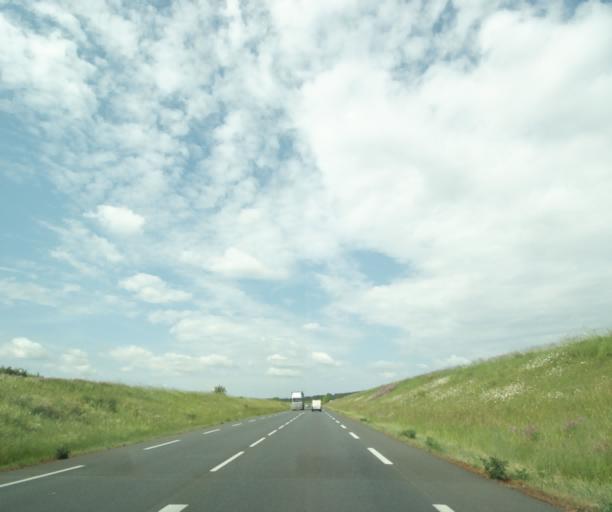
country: FR
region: Pays de la Loire
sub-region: Departement de Maine-et-Loire
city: Distre
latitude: 47.2259
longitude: -0.1158
